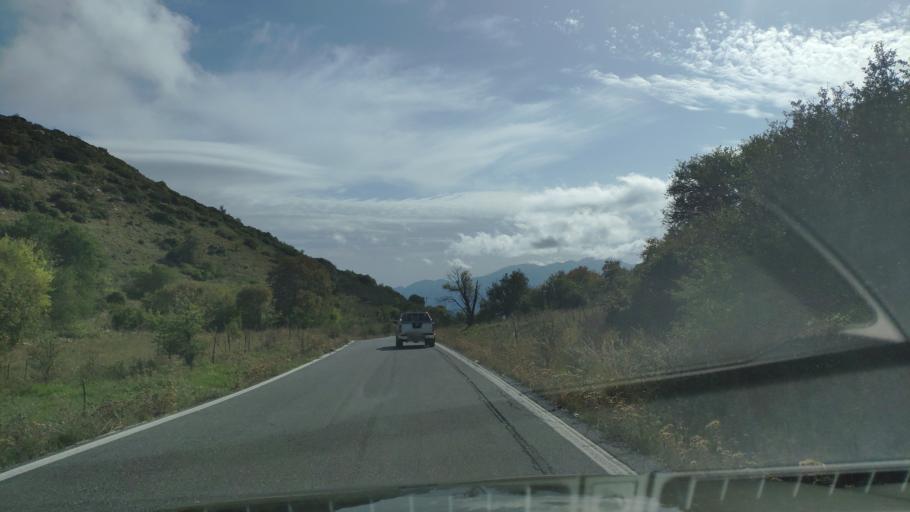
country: GR
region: Peloponnese
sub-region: Nomos Arkadias
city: Dimitsana
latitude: 37.5784
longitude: 22.0188
